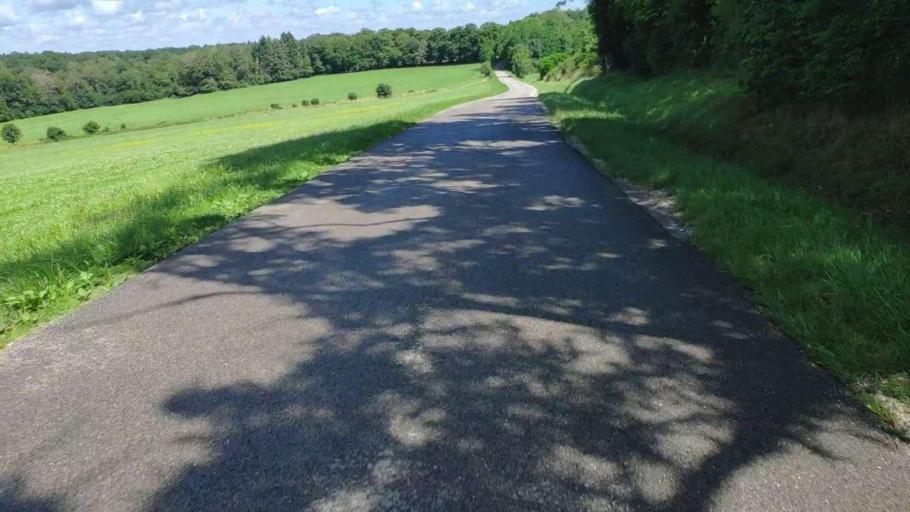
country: FR
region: Franche-Comte
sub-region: Departement du Jura
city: Bletterans
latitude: 46.8128
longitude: 5.5609
